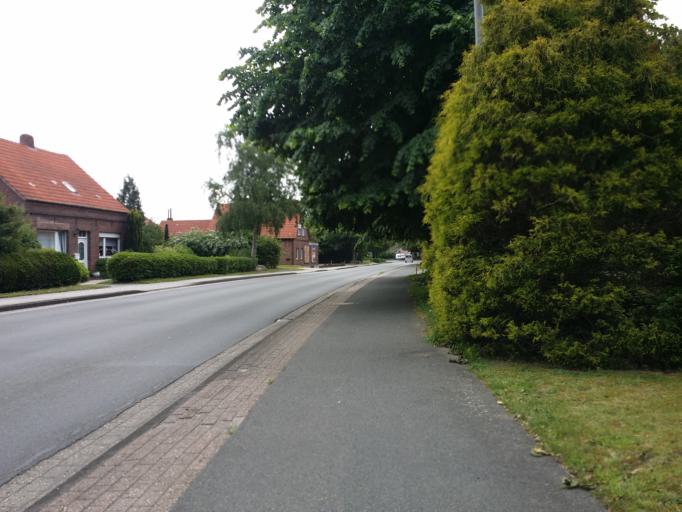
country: DE
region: Lower Saxony
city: Friedeburg
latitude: 53.4387
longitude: 7.8543
